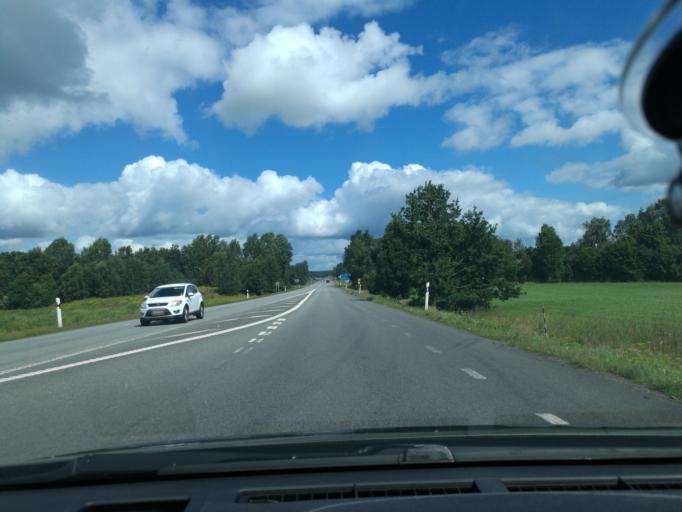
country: SE
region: Skane
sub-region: Hassleholms Kommun
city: Hassleholm
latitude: 56.1558
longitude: 13.8153
